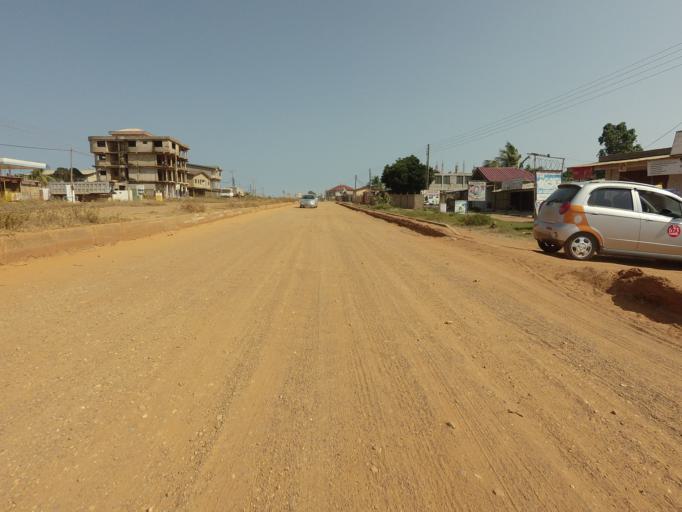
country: GH
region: Greater Accra
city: Teshi Old Town
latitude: 5.6145
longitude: -0.1244
